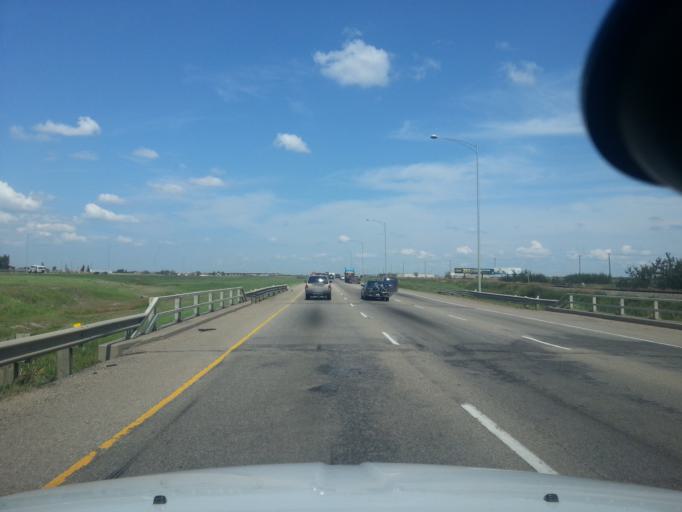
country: CA
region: Alberta
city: Beaumont
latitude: 53.3795
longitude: -113.5199
